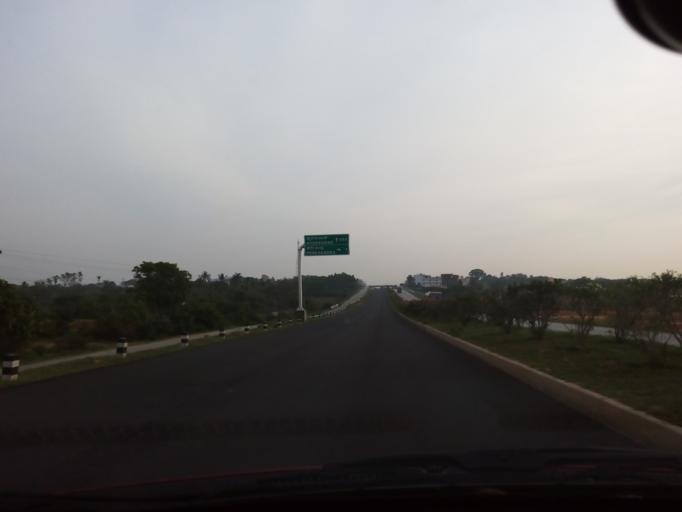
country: IN
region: Karnataka
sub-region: Chikkaballapur
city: Gudibanda
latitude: 13.5815
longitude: 77.7823
